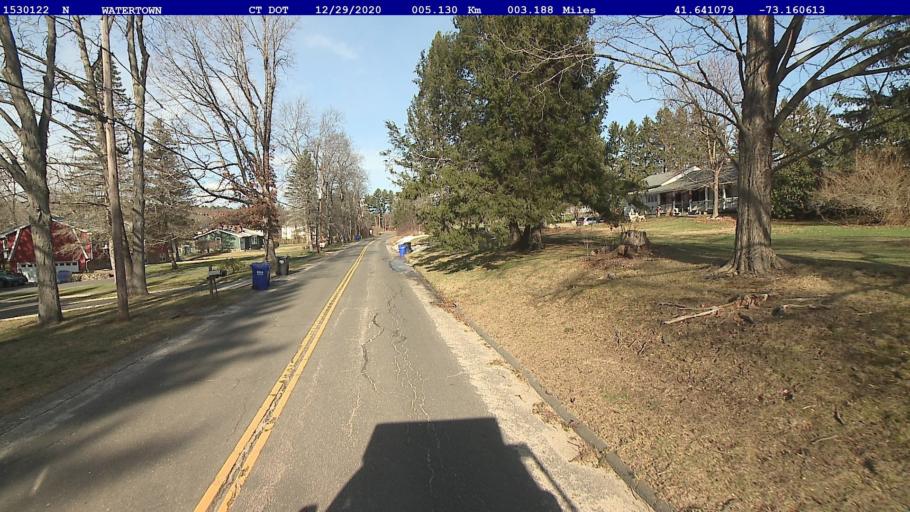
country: US
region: Connecticut
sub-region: Litchfield County
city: Bethlehem Village
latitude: 41.6411
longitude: -73.1606
